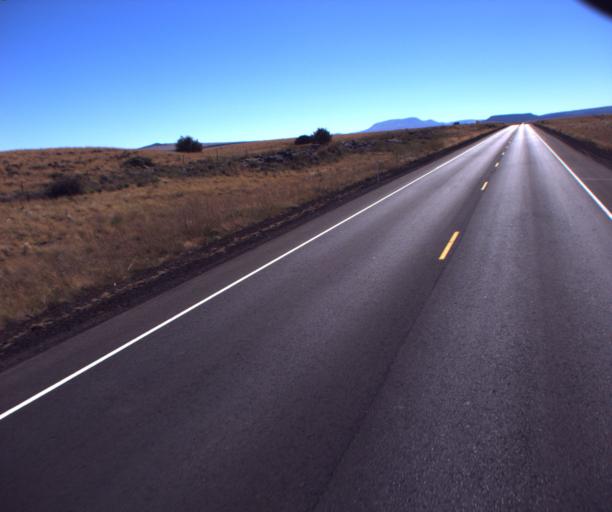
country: US
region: Arizona
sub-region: Apache County
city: Springerville
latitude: 34.2278
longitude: -109.3394
